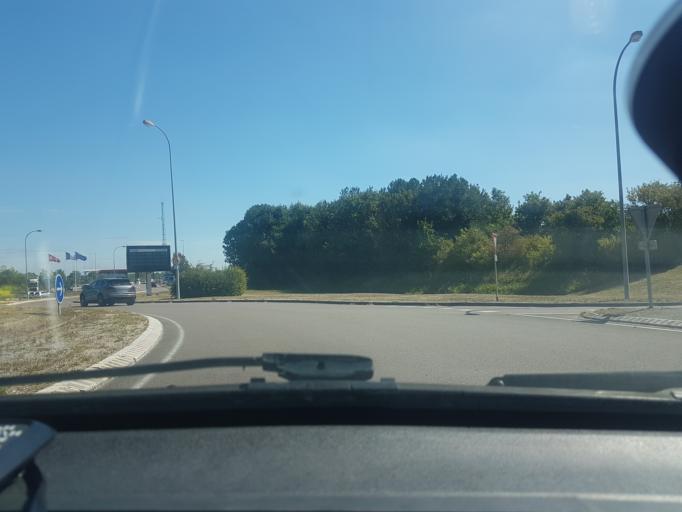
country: FR
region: Bourgogne
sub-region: Departement de la Cote-d'Or
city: Couternon
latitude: 47.3445
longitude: 5.1559
